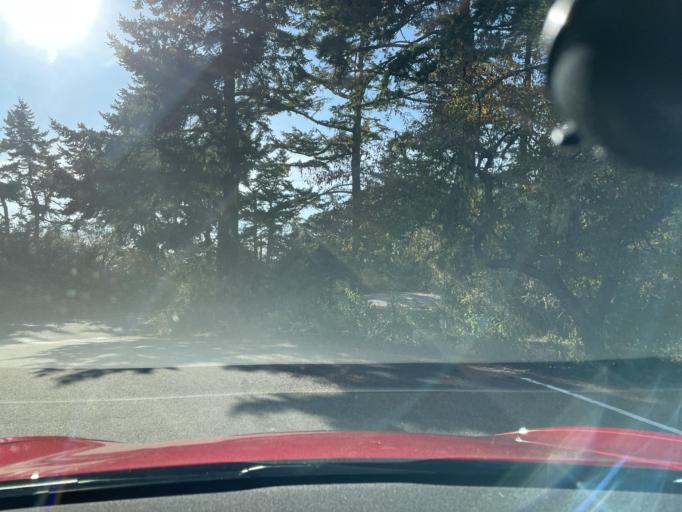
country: US
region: Washington
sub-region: San Juan County
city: Friday Harbor
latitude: 48.4647
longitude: -123.0247
